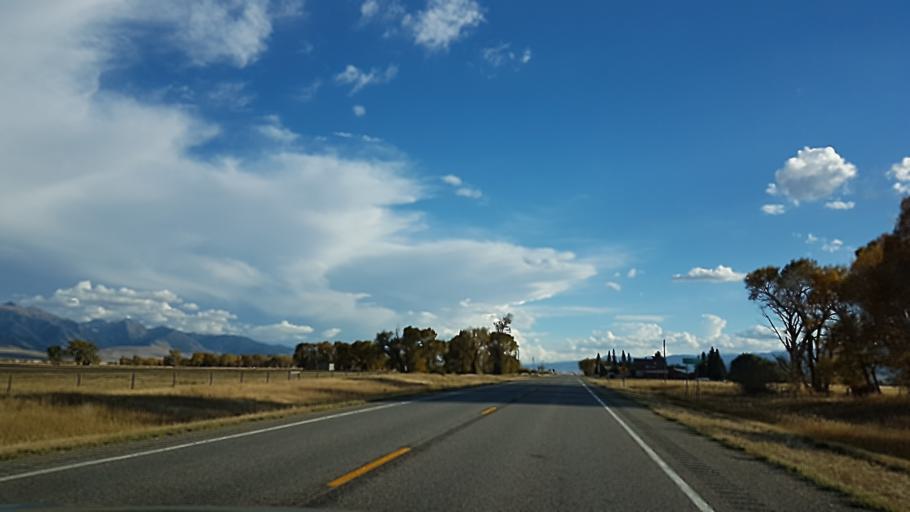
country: US
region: Montana
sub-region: Madison County
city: Virginia City
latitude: 45.2061
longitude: -111.6788
